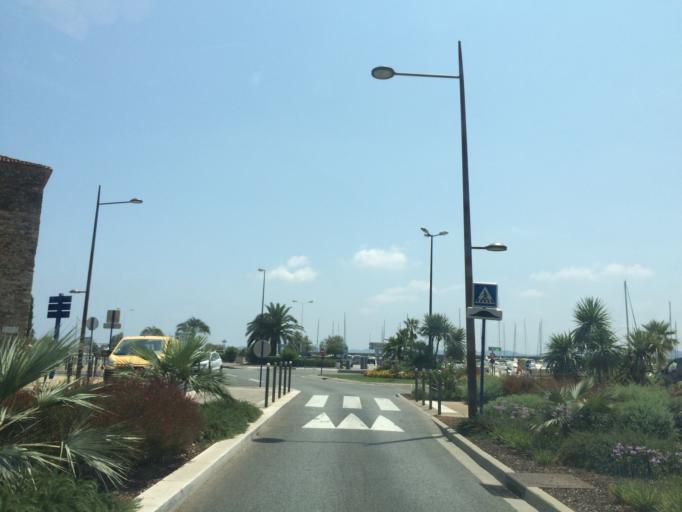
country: FR
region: Provence-Alpes-Cote d'Azur
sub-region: Departement du Var
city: Sainte-Maxime
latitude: 43.3070
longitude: 6.6404
